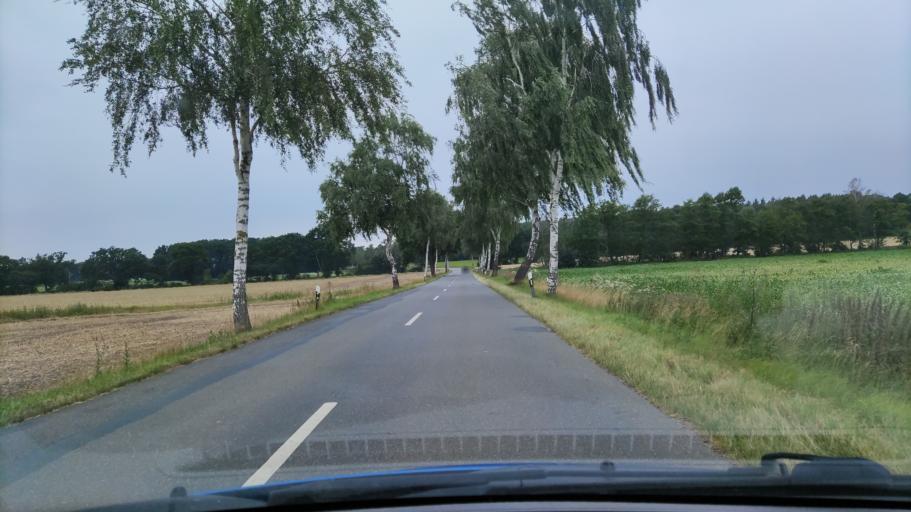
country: DE
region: Lower Saxony
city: Rosche
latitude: 52.9812
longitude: 10.7782
